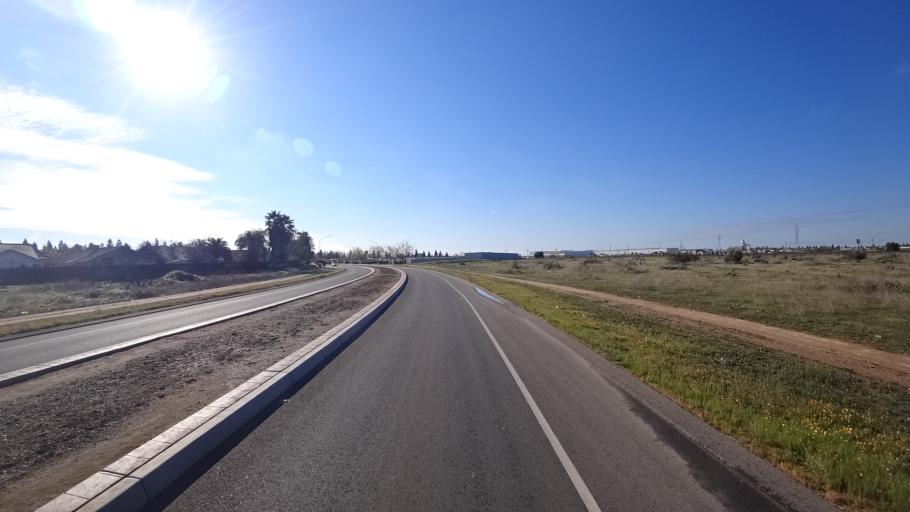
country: US
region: California
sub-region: Fresno County
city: Biola
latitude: 36.8252
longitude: -119.8971
